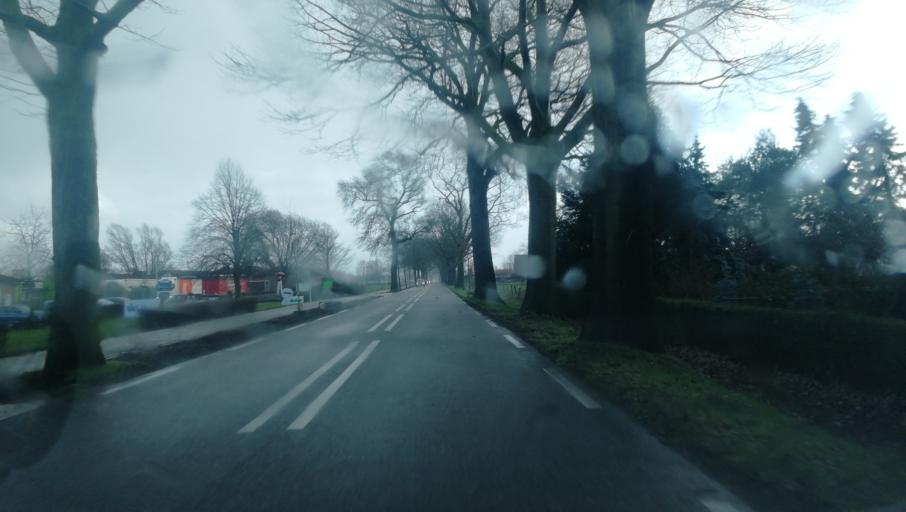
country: NL
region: Limburg
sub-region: Gemeente Peel en Maas
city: Maasbree
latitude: 51.4306
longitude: 6.0943
